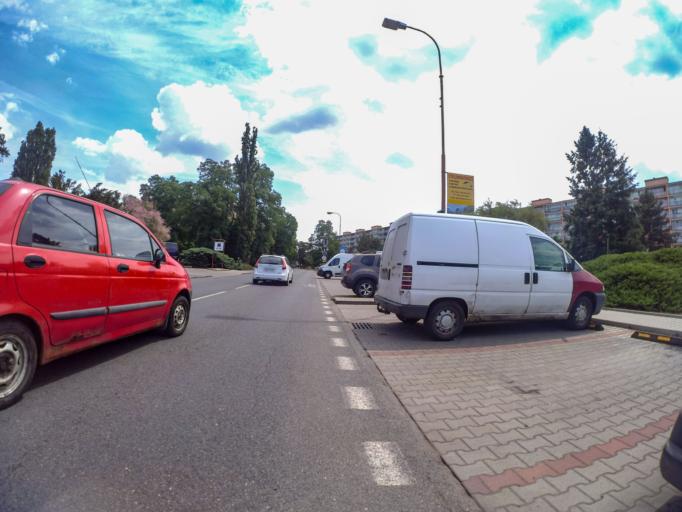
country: CZ
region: Central Bohemia
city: Neratovice
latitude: 50.2586
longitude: 14.5181
